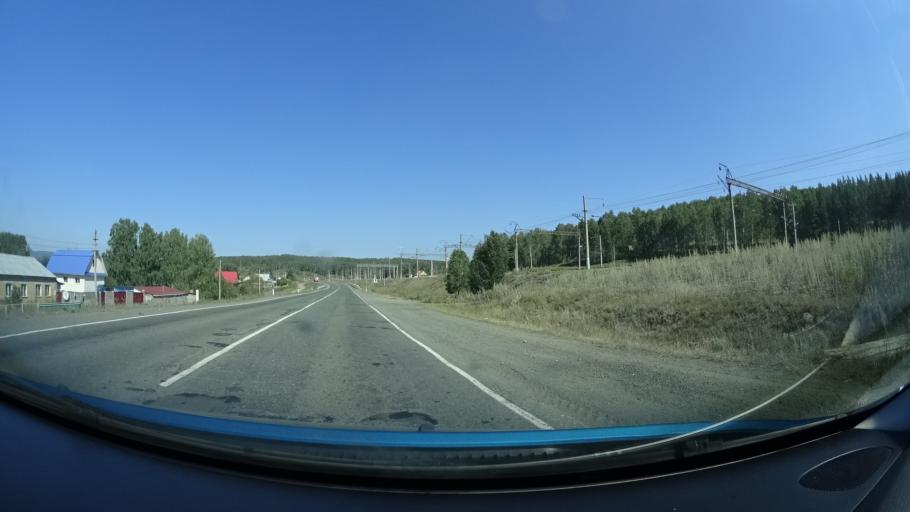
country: RU
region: Bashkortostan
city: Abzakovo
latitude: 53.8146
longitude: 58.6424
